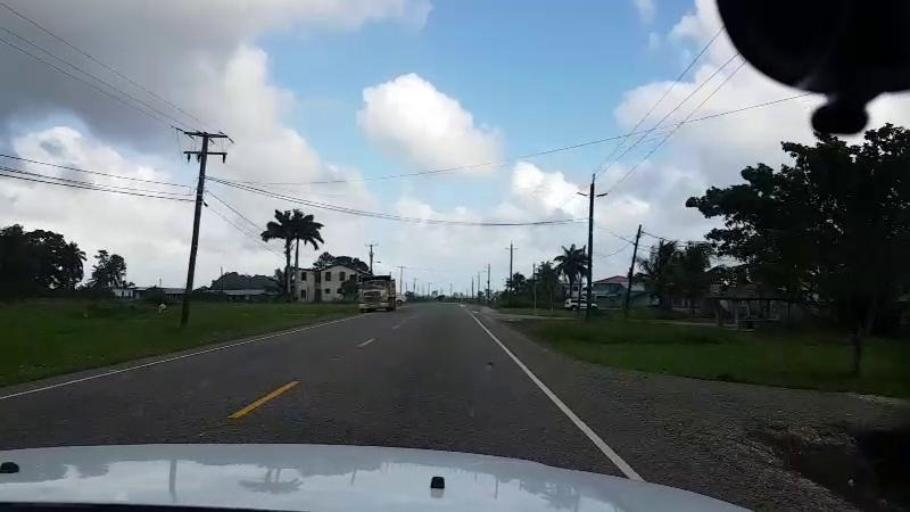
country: BZ
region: Stann Creek
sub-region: Dangriga
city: Dangriga
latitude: 16.9947
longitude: -88.3689
